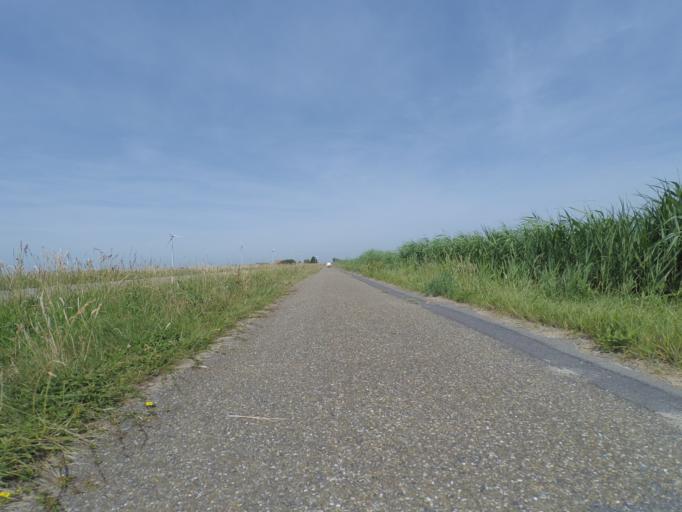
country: NL
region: Zeeland
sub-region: Schouwen-Duiveland
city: Bruinisse
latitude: 51.6304
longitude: 4.1333
